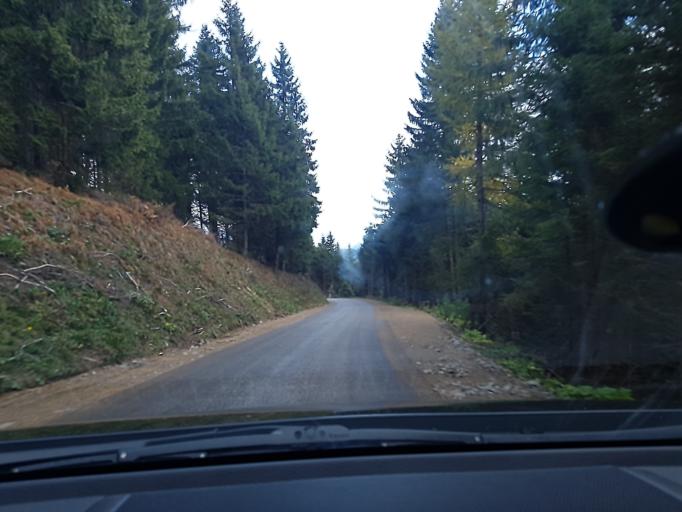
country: AT
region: Styria
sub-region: Politischer Bezirk Murtal
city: Oberzeiring
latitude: 47.2647
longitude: 14.4425
